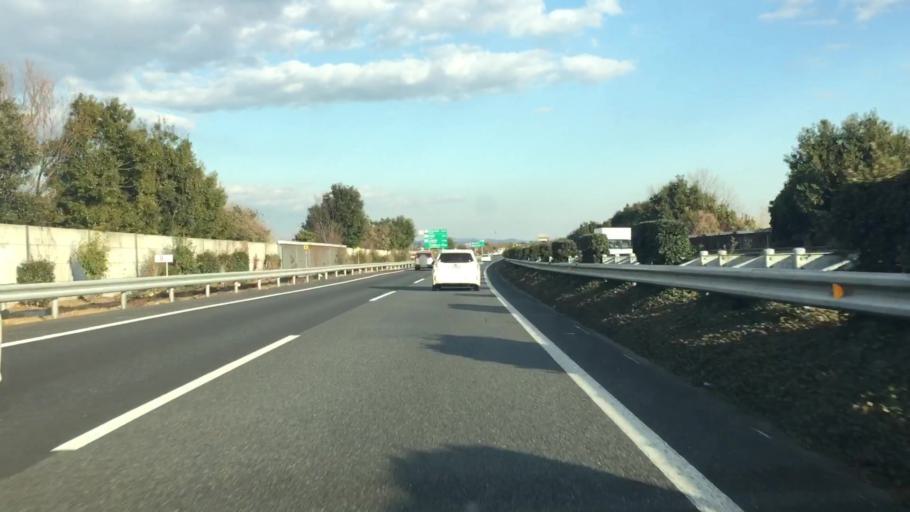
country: JP
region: Gunma
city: Isesaki
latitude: 36.3510
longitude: 139.1522
